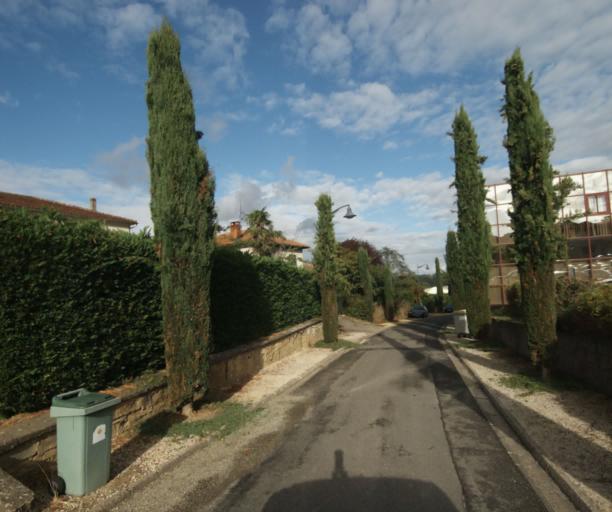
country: FR
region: Midi-Pyrenees
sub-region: Departement du Gers
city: Eauze
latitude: 43.8623
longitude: 0.1019
